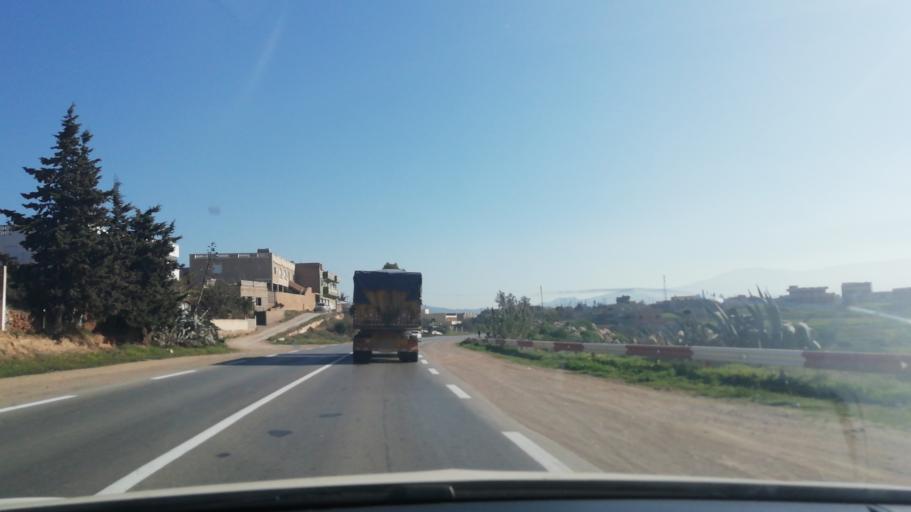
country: DZ
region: Tlemcen
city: Nedroma
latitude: 35.0882
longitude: -1.8075
